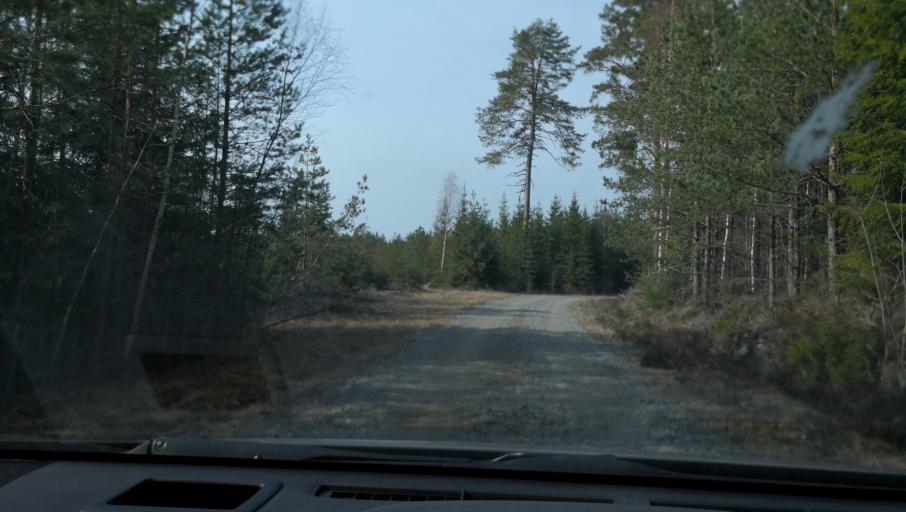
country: SE
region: OErebro
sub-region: Lindesbergs Kommun
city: Frovi
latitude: 59.3831
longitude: 15.4109
